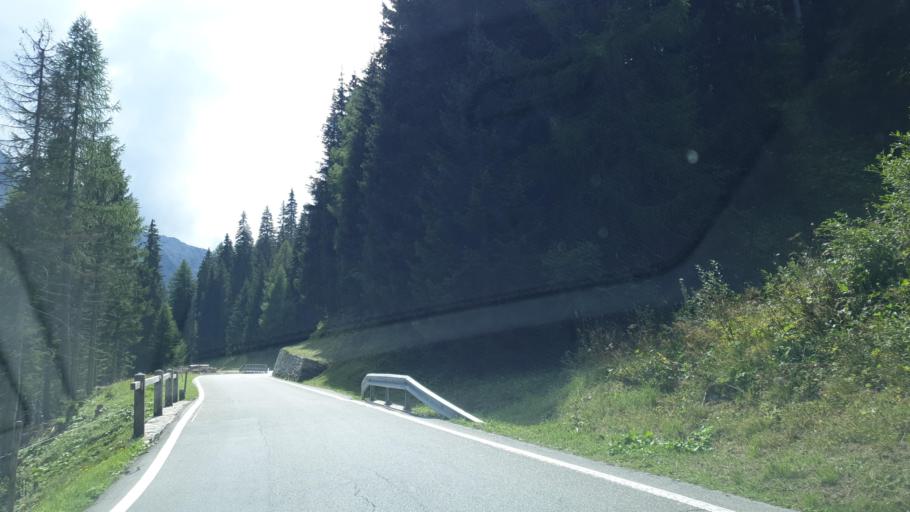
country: CH
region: Grisons
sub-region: Hinterrhein District
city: Hinterrhein
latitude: 46.5402
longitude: 9.3242
